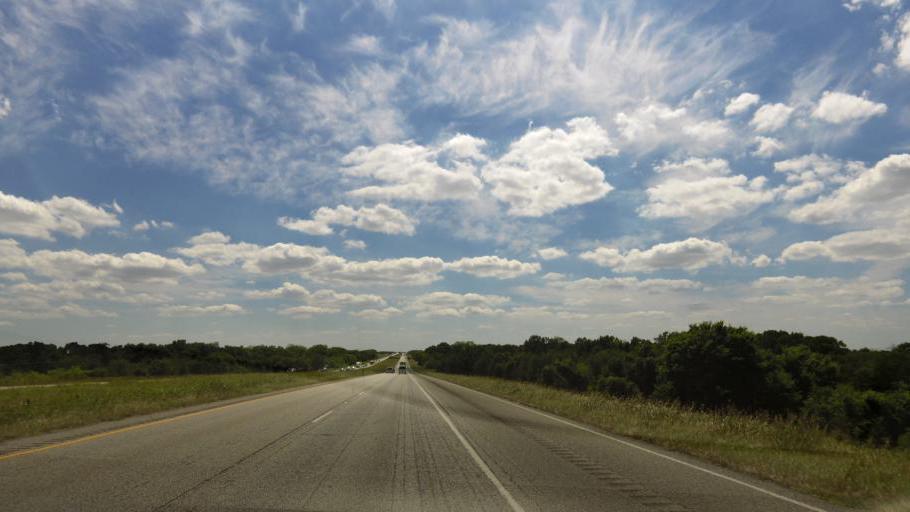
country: US
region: Texas
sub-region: Gonzales County
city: Waelder
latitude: 29.6821
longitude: -97.2702
